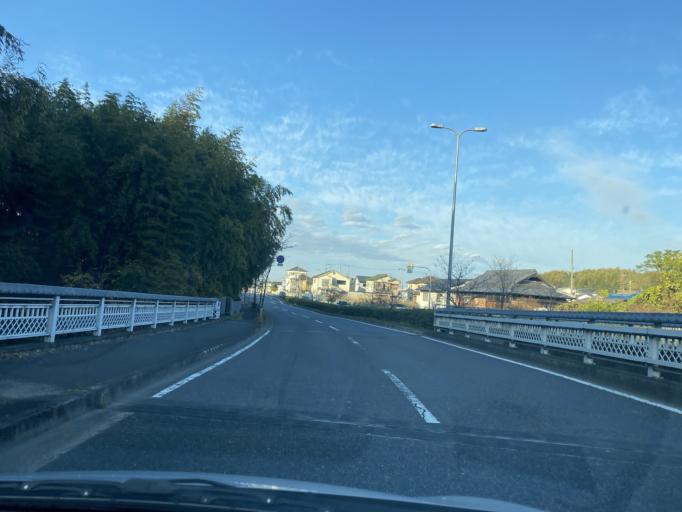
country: JP
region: Osaka
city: Izumi
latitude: 34.4249
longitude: 135.4401
